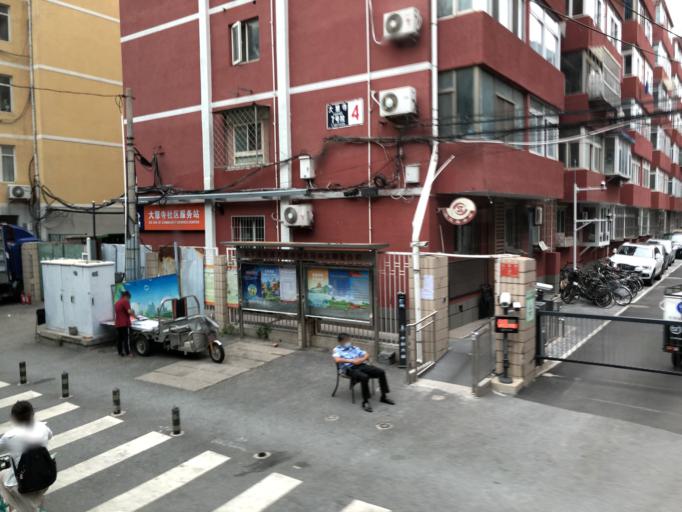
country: CN
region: Beijing
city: Haidian
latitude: 39.9505
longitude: 116.3208
